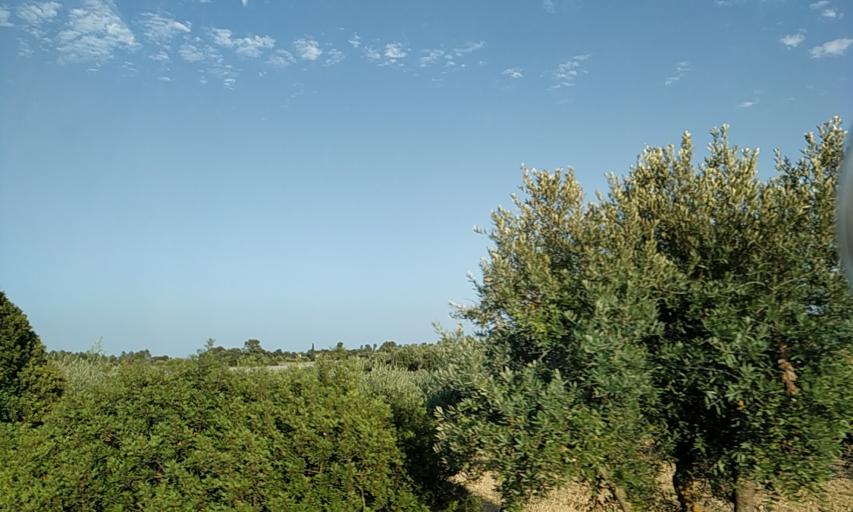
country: PT
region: Santarem
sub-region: Alcanena
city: Alcanena
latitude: 39.4317
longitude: -8.6311
